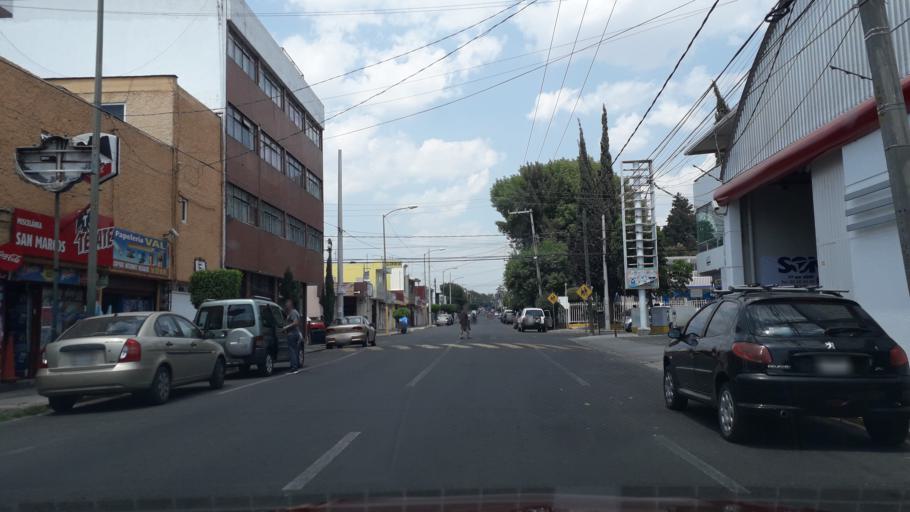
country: MX
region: Puebla
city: Puebla
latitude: 19.0333
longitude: -98.2208
